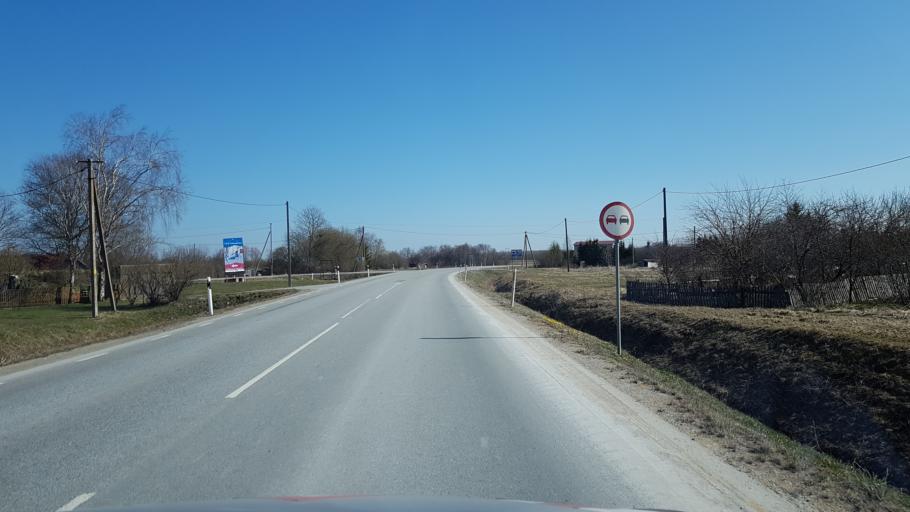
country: EE
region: Ida-Virumaa
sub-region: Kivioli linn
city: Kivioli
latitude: 59.3638
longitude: 26.9636
